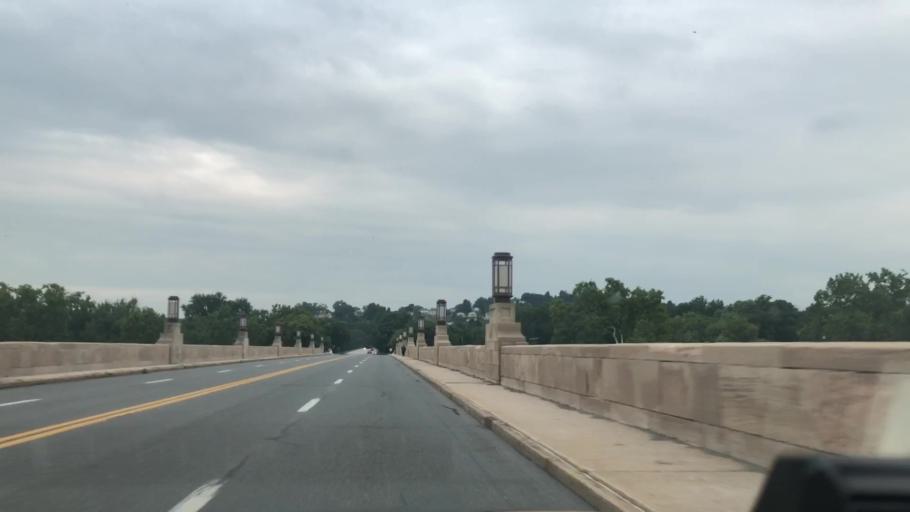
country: US
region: Pennsylvania
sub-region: Dauphin County
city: Harrisburg
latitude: 40.2565
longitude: -76.8849
